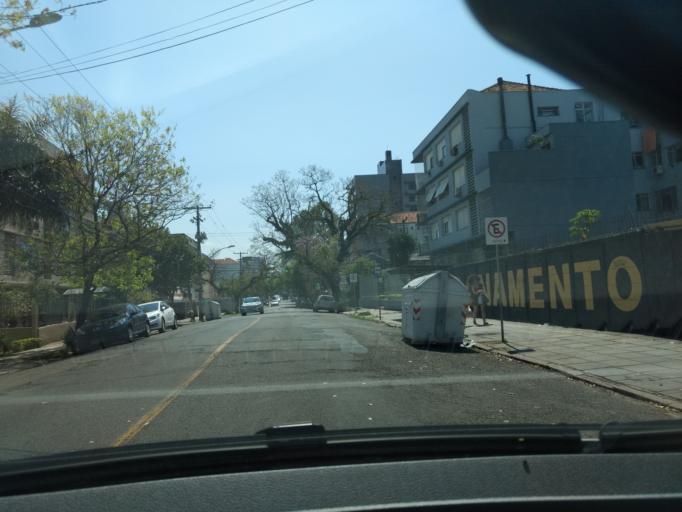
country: BR
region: Rio Grande do Sul
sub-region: Porto Alegre
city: Porto Alegre
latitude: -30.0434
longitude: -51.2112
